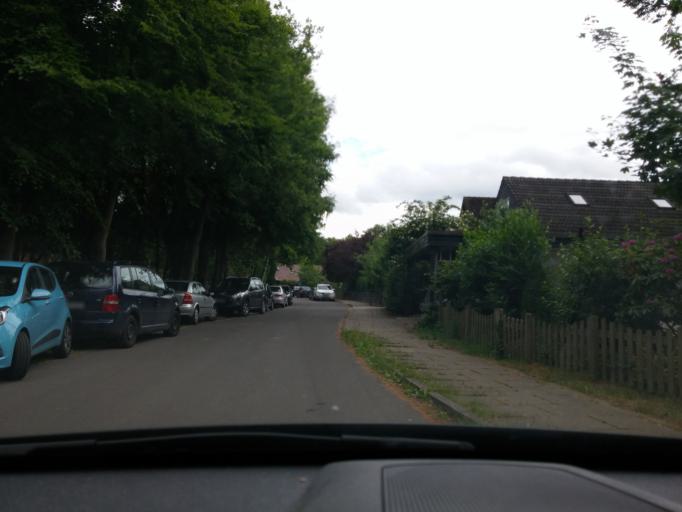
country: DE
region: Lower Saxony
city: Jesteburg
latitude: 53.3042
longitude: 9.9573
